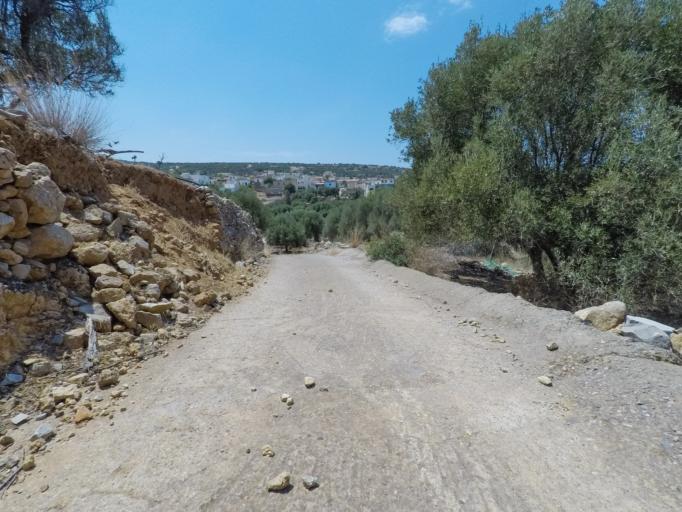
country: GR
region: Crete
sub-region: Nomos Lasithiou
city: Elounda
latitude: 35.3158
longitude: 25.7364
